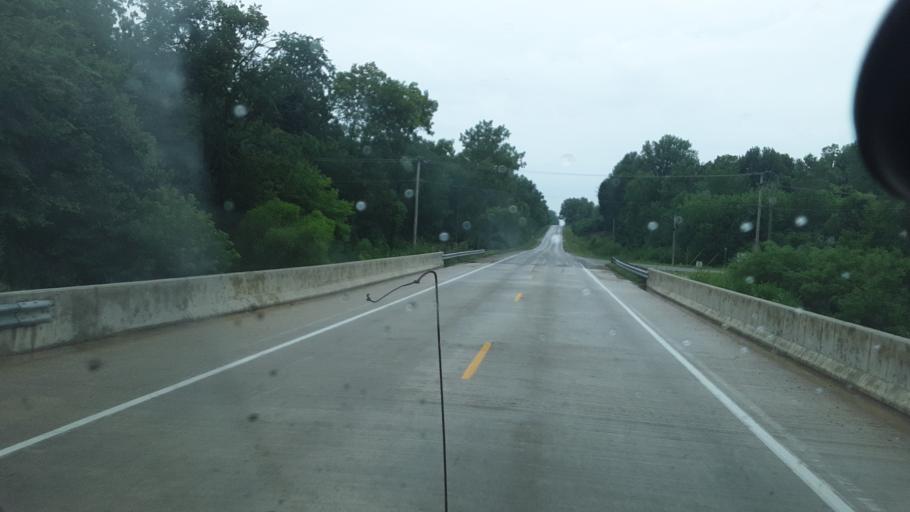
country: US
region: Indiana
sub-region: Steuben County
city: Hamilton
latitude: 41.5589
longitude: -84.8350
